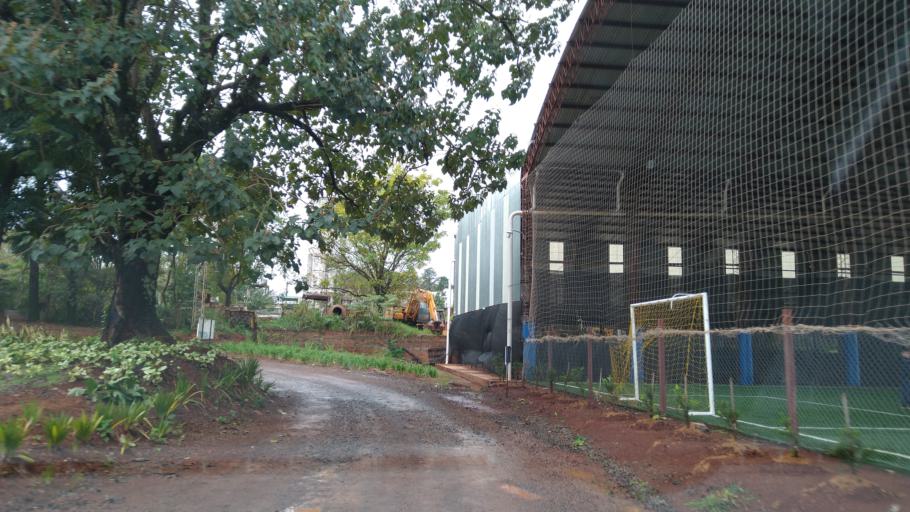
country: AR
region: Misiones
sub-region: Departamento de Capital
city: Posadas
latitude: -27.4006
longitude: -55.9410
